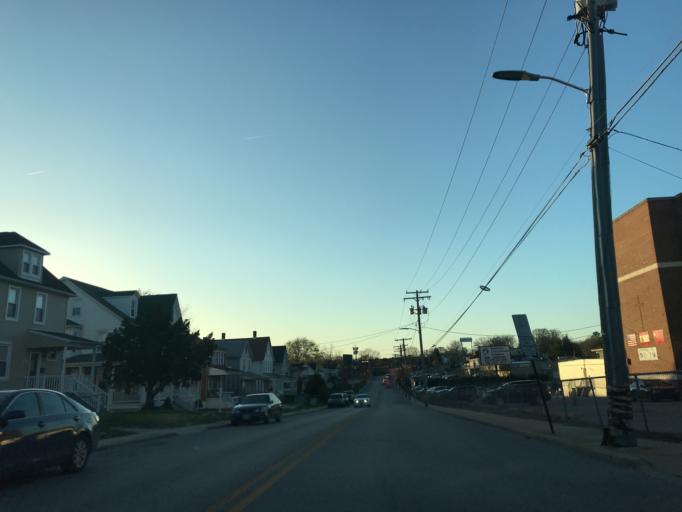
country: US
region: Maryland
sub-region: Baltimore County
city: Rosedale
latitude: 39.3354
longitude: -76.5487
